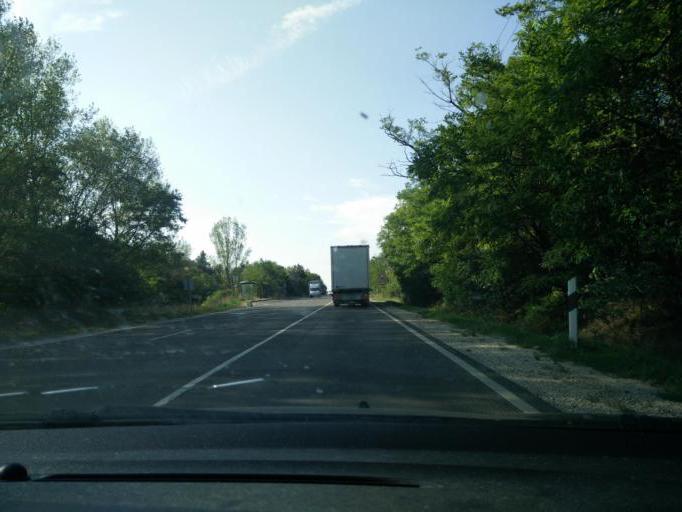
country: HU
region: Pest
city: Piliscsaba
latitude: 47.6231
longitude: 18.8635
